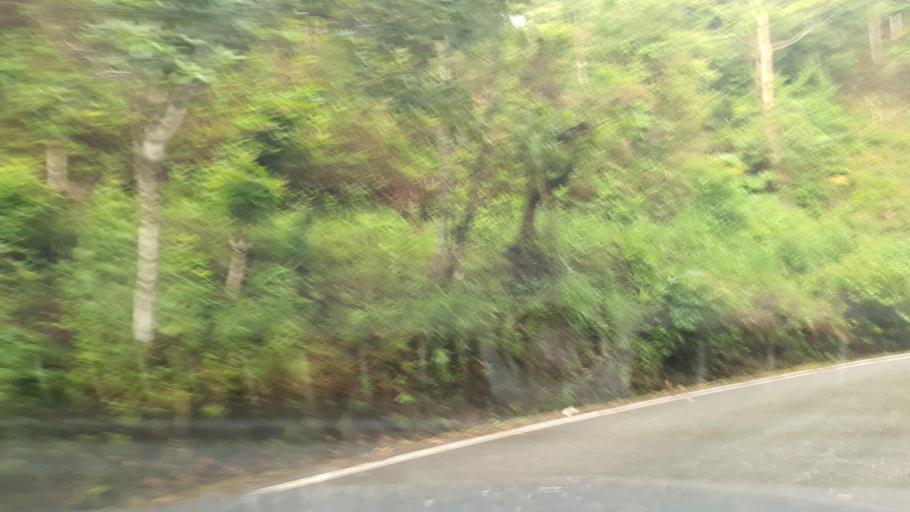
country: TH
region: Mae Hong Son
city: Mae Hi
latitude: 19.2549
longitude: 98.6465
